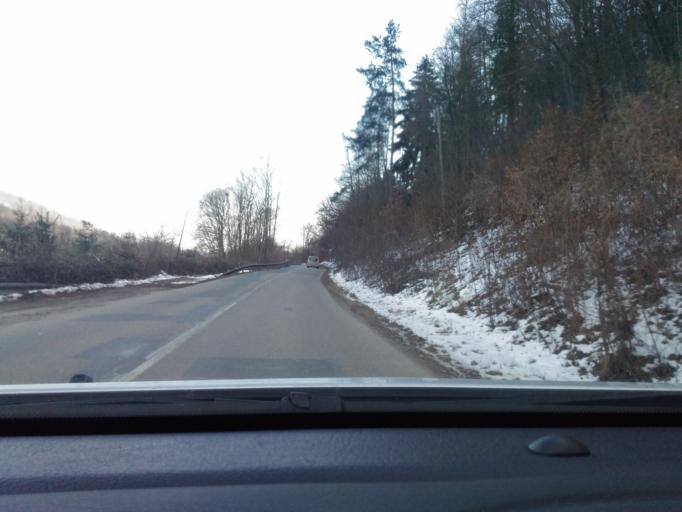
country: CZ
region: South Moravian
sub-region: Okres Brno-Venkov
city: Dolni Loucky
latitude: 49.3783
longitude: 16.3800
